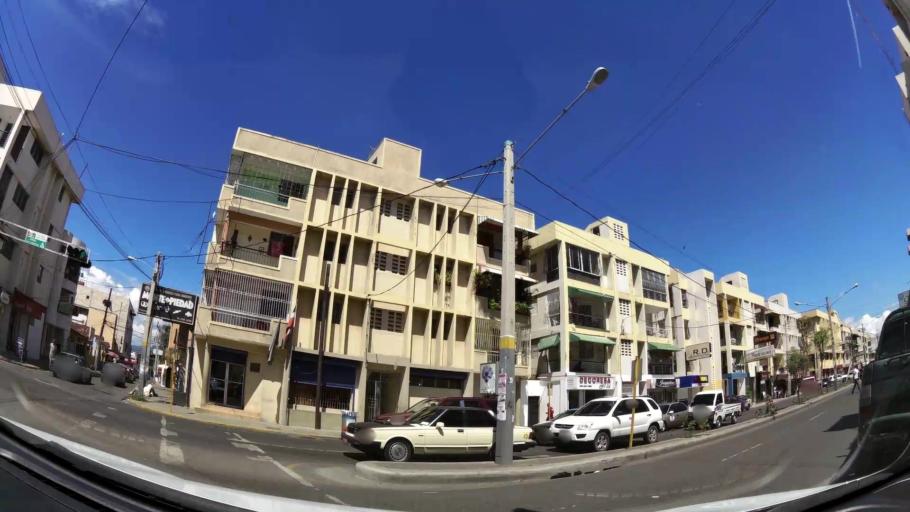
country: DO
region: Santiago
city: Santiago de los Caballeros
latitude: 19.4547
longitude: -70.7032
